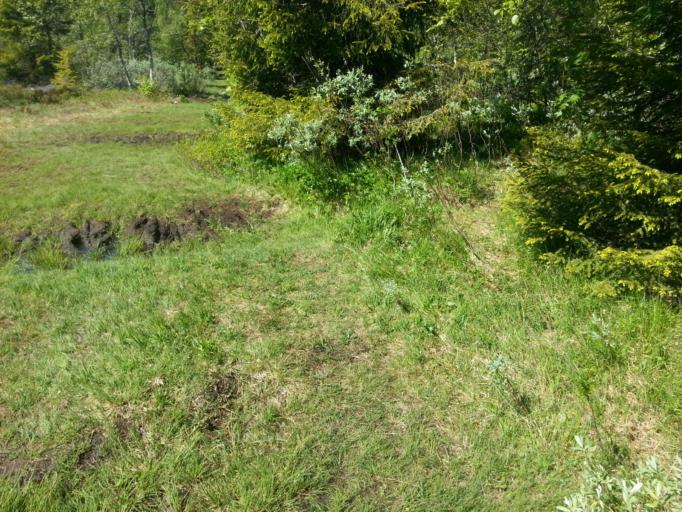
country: NO
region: Sor-Trondelag
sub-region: Trondheim
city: Trondheim
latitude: 63.4018
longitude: 10.2896
